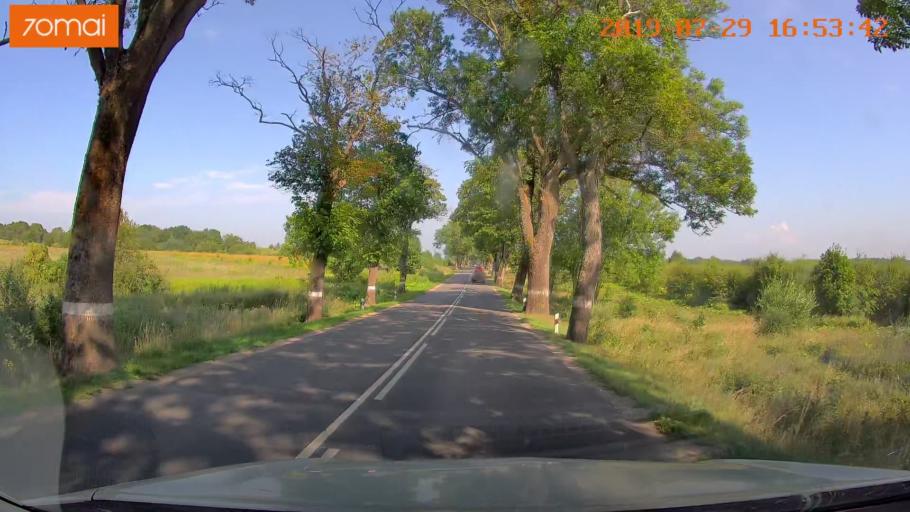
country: RU
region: Kaliningrad
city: Otradnoye
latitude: 54.8132
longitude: 20.1149
